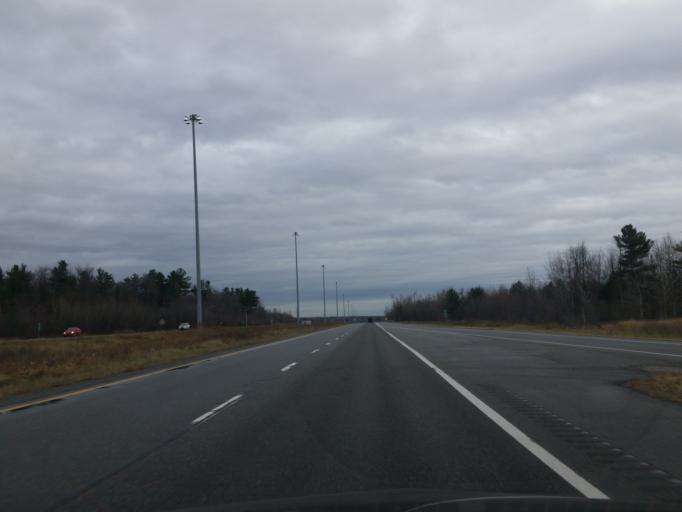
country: CA
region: Ontario
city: Clarence-Rockland
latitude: 45.5554
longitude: -75.4172
